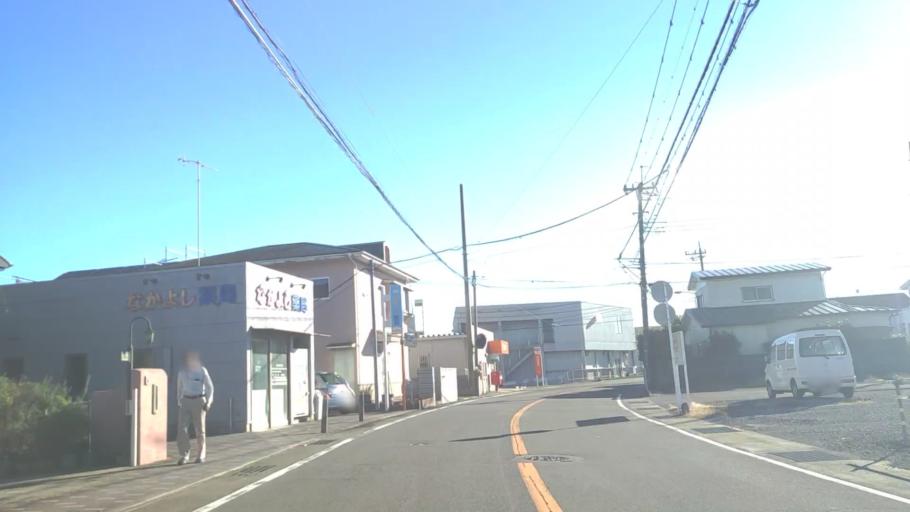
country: JP
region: Kanagawa
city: Atsugi
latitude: 35.4136
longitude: 139.3655
